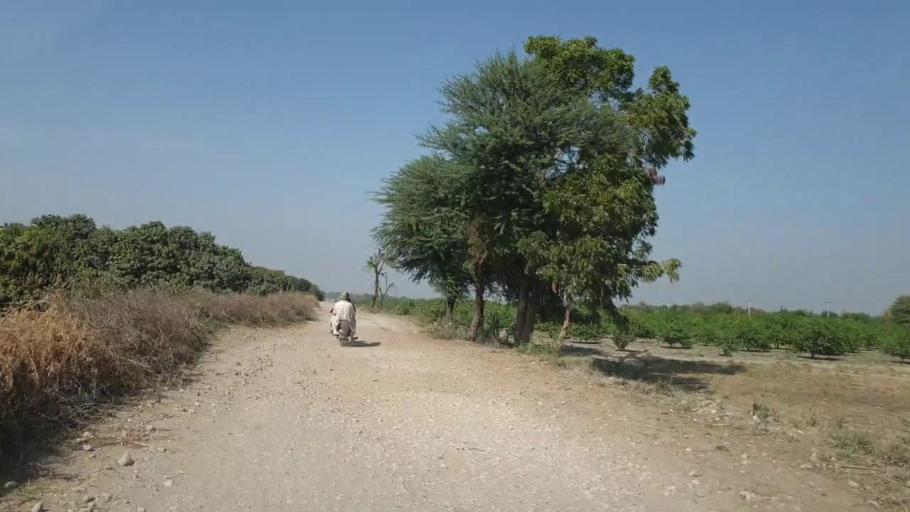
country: PK
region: Sindh
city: Nabisar
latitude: 25.0262
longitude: 69.5244
